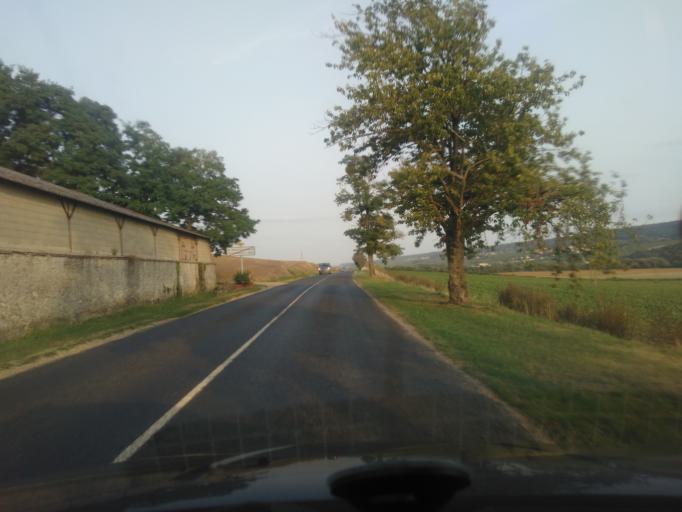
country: FR
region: Champagne-Ardenne
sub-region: Departement de la Marne
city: Mareuil-le-Port
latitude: 49.0904
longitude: 3.7669
